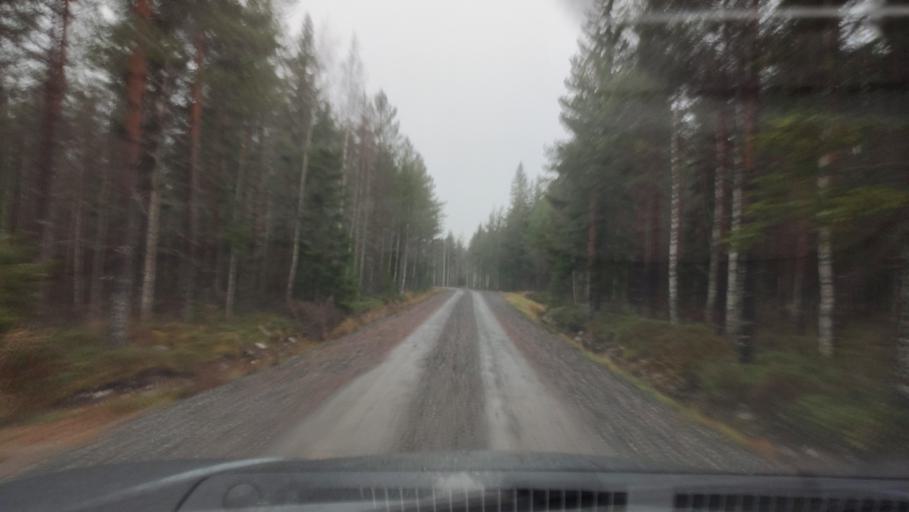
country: FI
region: Southern Ostrobothnia
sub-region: Suupohja
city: Karijoki
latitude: 62.1781
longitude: 21.6961
